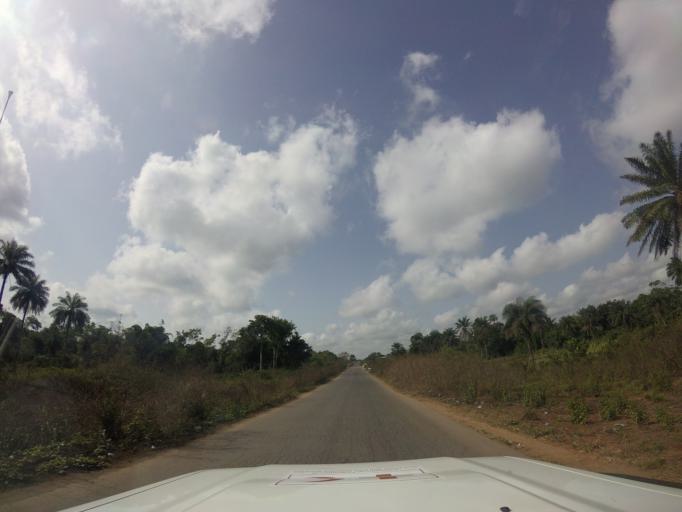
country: LR
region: Bomi
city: Tubmanburg
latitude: 6.6918
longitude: -10.8745
